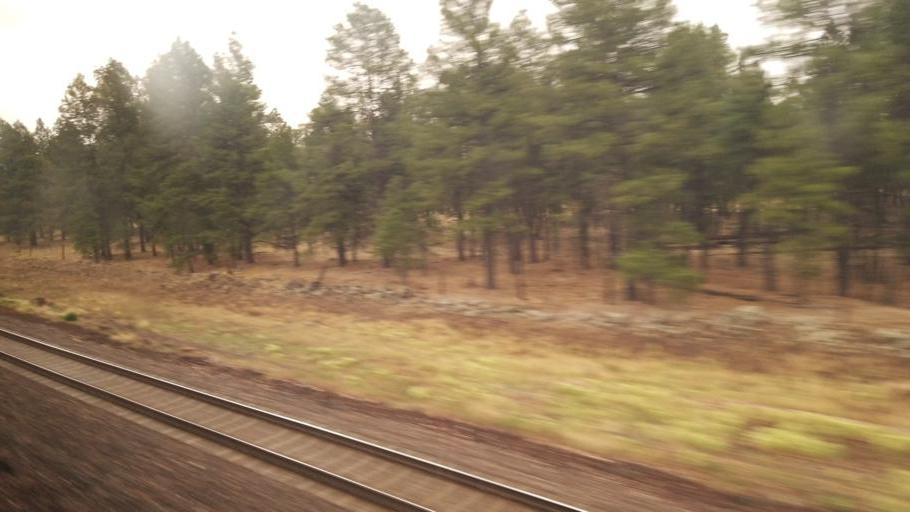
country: US
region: Arizona
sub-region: Coconino County
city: Parks
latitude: 35.2403
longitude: -111.9938
